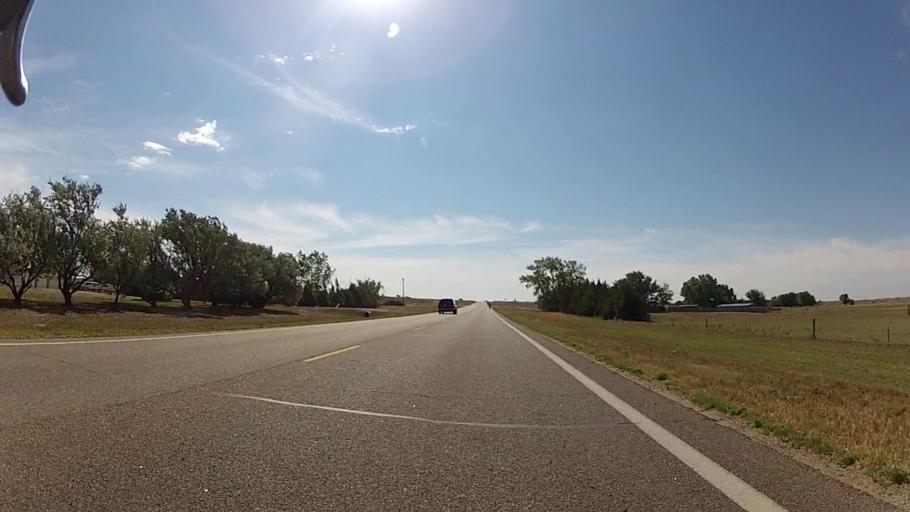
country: US
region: Kansas
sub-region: Grant County
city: Ulysses
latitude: 37.5700
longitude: -101.3289
